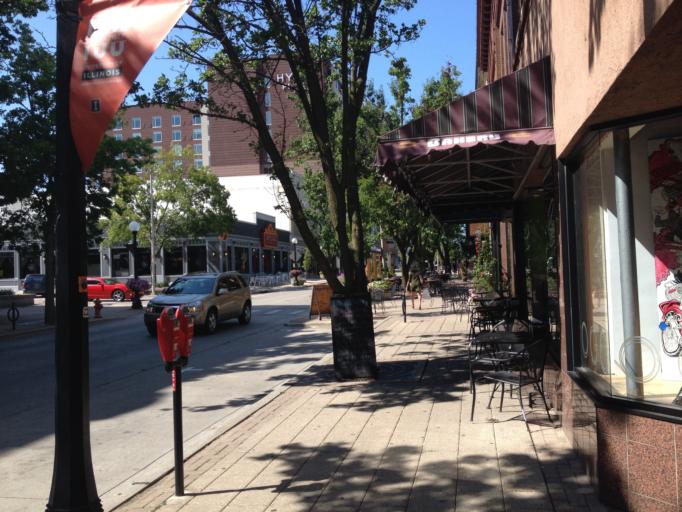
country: US
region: Illinois
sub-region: Champaign County
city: Champaign
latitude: 40.1168
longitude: -88.2437
